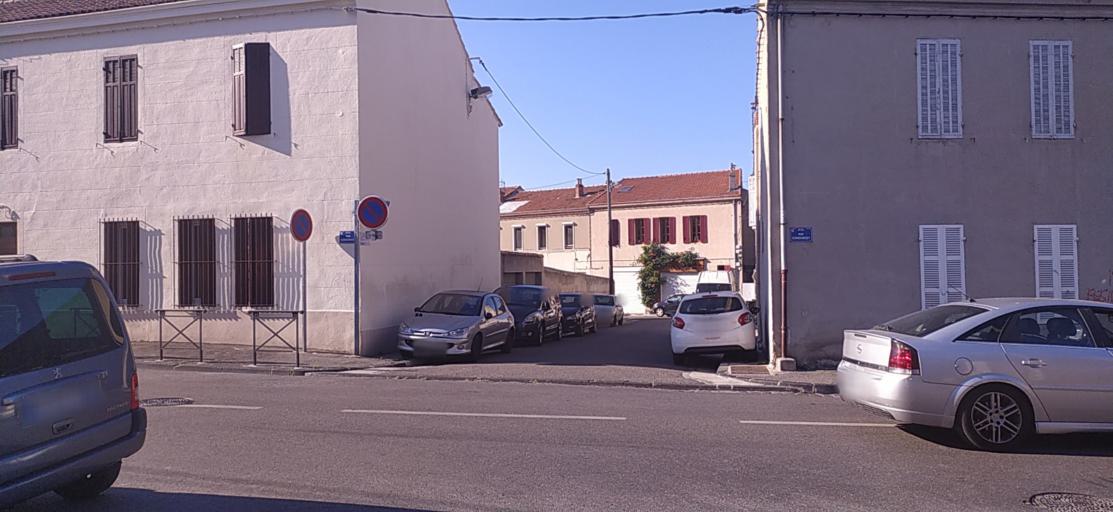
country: FR
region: Provence-Alpes-Cote d'Azur
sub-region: Departement des Bouches-du-Rhone
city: Marseille 16
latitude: 43.3578
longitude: 5.3390
